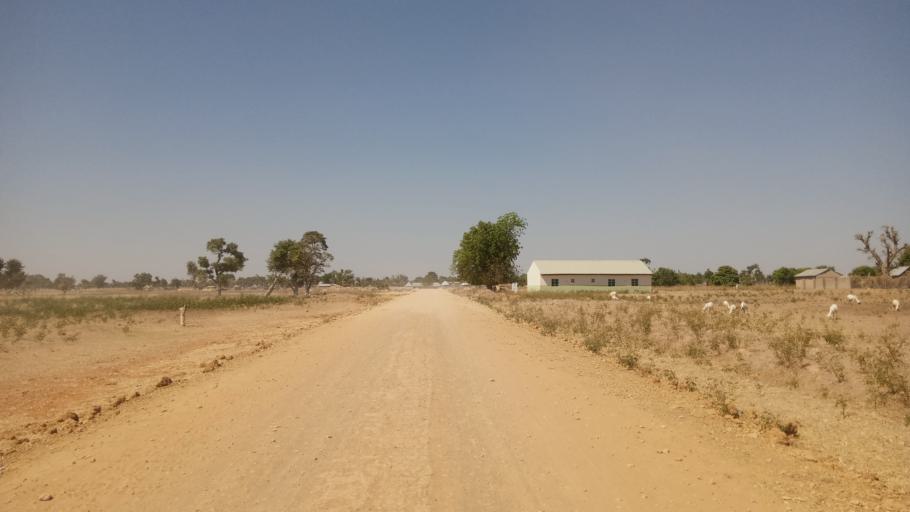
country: NG
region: Adamawa
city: Ngurore
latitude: 9.2977
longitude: 12.1405
